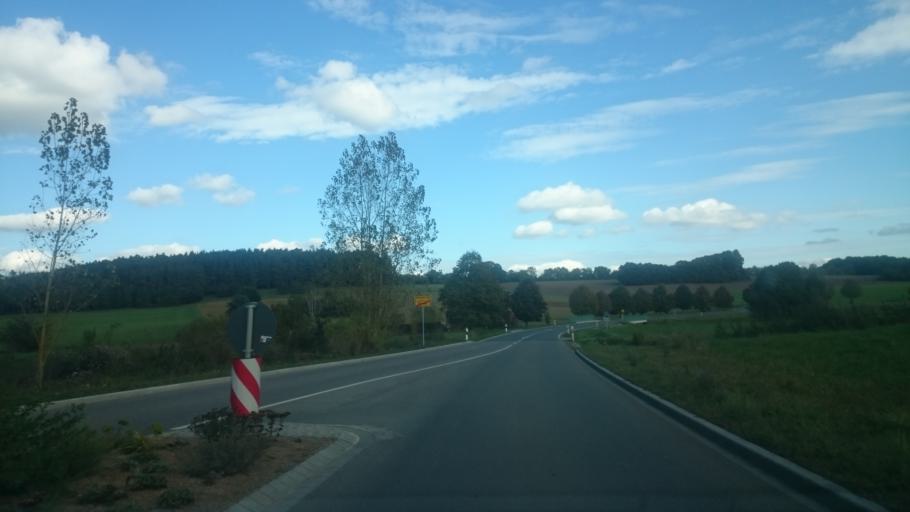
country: DE
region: Bavaria
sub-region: Regierungsbezirk Mittelfranken
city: Hilpoltstein
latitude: 49.1499
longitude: 11.2189
